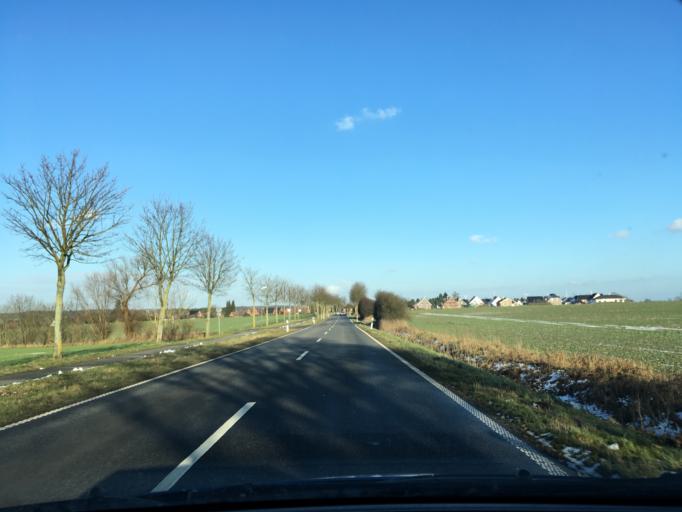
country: DE
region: Schleswig-Holstein
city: Krukow
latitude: 53.4375
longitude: 10.4768
